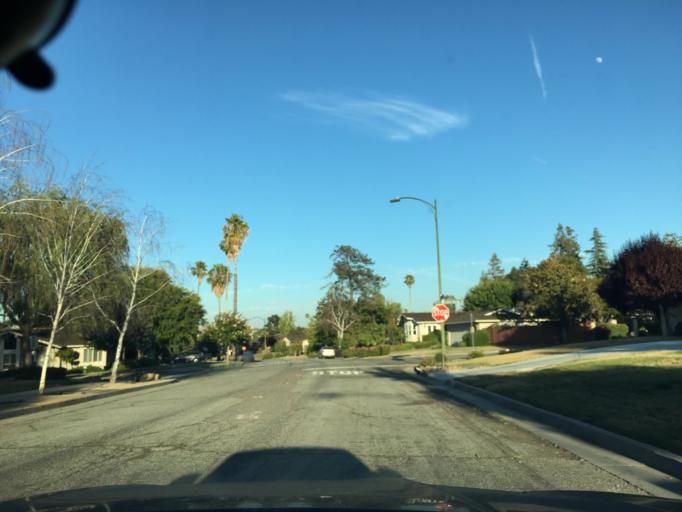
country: US
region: California
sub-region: Santa Clara County
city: Cambrian Park
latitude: 37.2192
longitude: -121.8742
